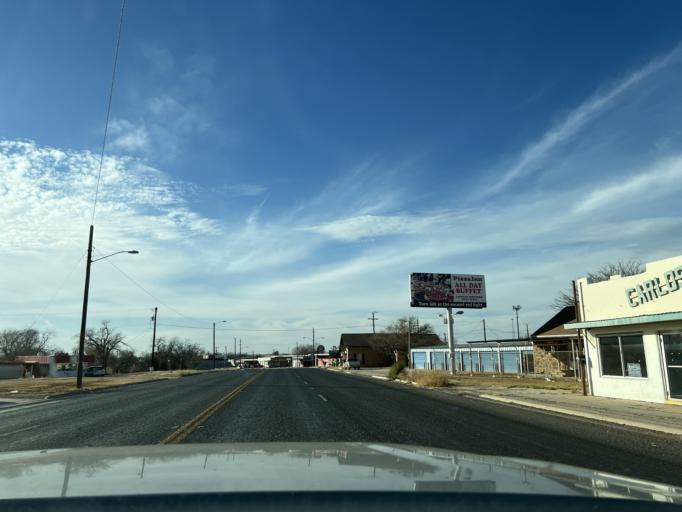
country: US
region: Texas
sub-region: Scurry County
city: Snyder
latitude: 32.7163
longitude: -100.9033
